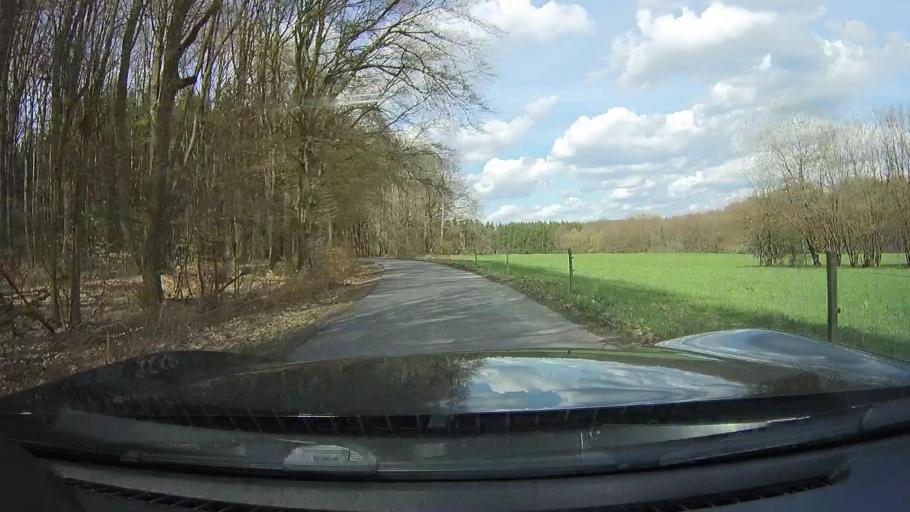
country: DE
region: Hesse
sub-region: Regierungsbezirk Darmstadt
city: Hesseneck
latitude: 49.5866
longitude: 9.0895
